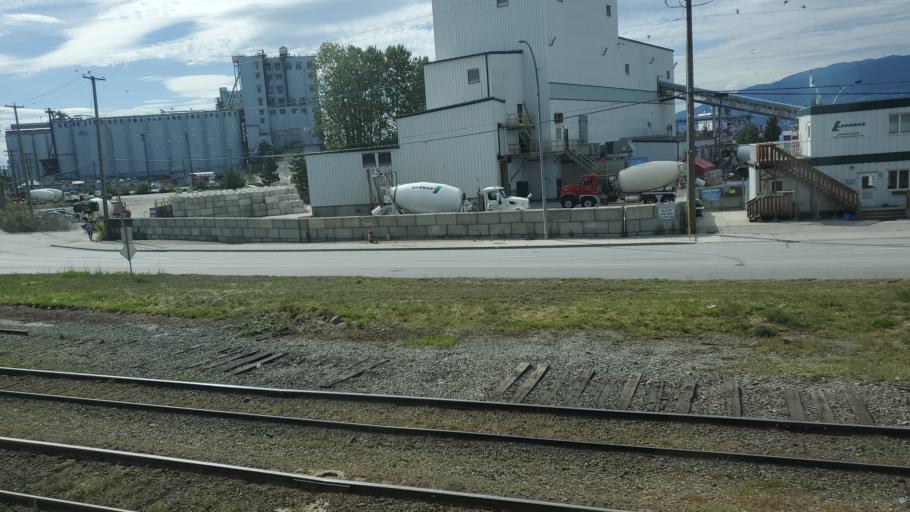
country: CA
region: British Columbia
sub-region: Fraser Valley Regional District
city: North Vancouver
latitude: 49.2862
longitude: -123.0627
